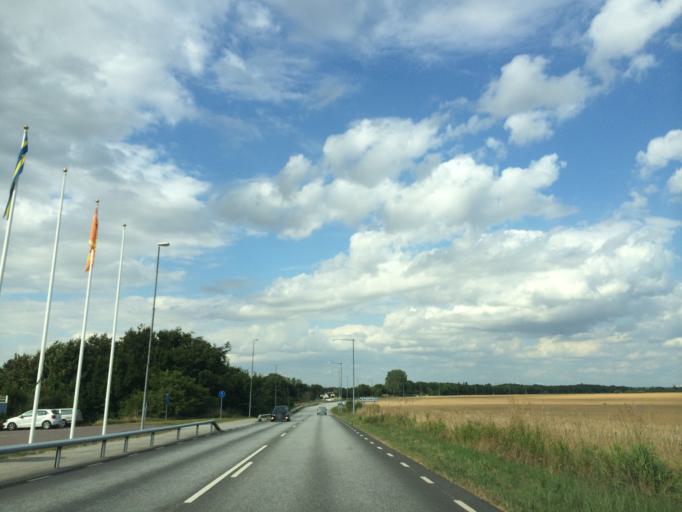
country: SE
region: Skane
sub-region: Lomma Kommun
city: Lomma
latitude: 55.6573
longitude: 13.0571
